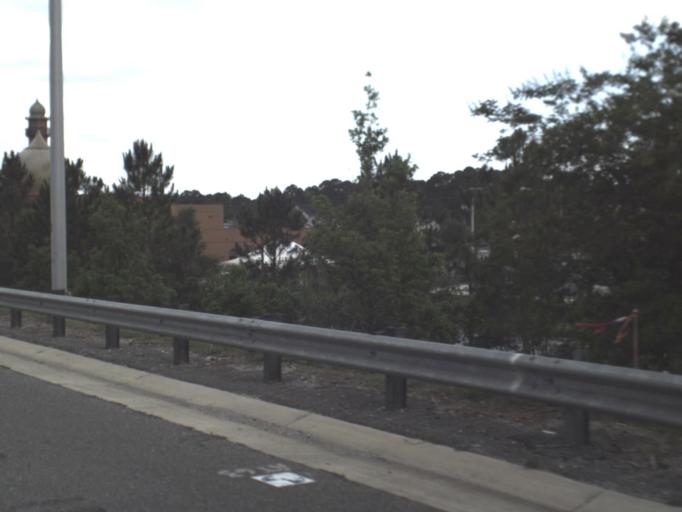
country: US
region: Florida
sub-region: Duval County
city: Neptune Beach
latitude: 30.3084
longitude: -81.5239
